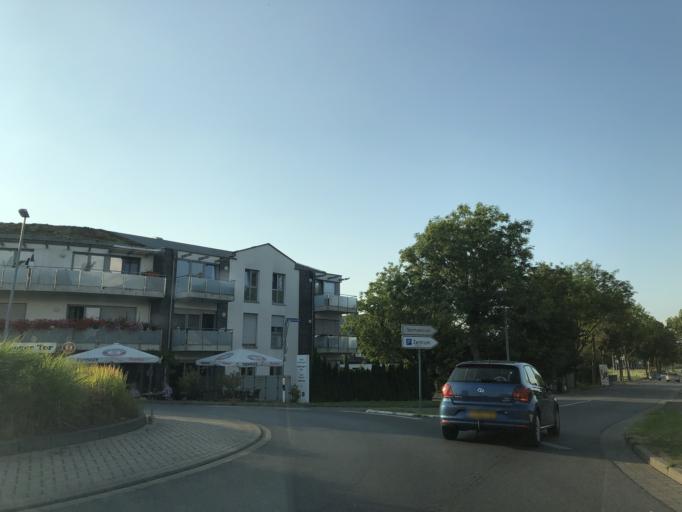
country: DE
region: North Rhine-Westphalia
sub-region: Regierungsbezirk Dusseldorf
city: Kranenburg
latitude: 51.7906
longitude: 6.0045
